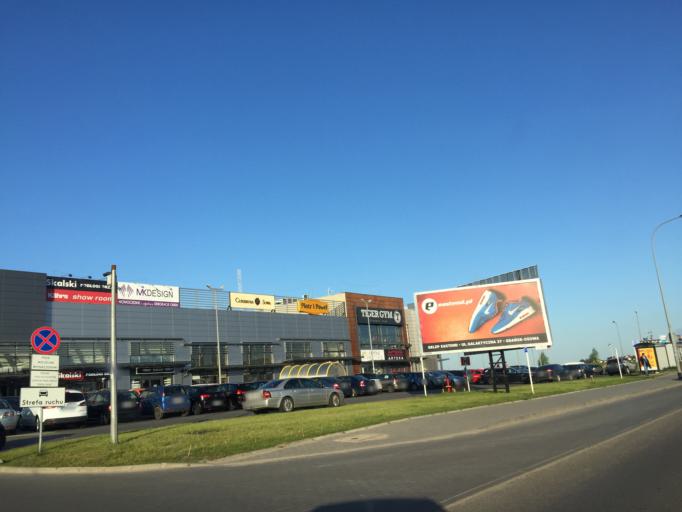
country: PL
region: Pomeranian Voivodeship
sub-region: Powiat gdanski
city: Kowale
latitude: 54.3228
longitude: 18.5516
